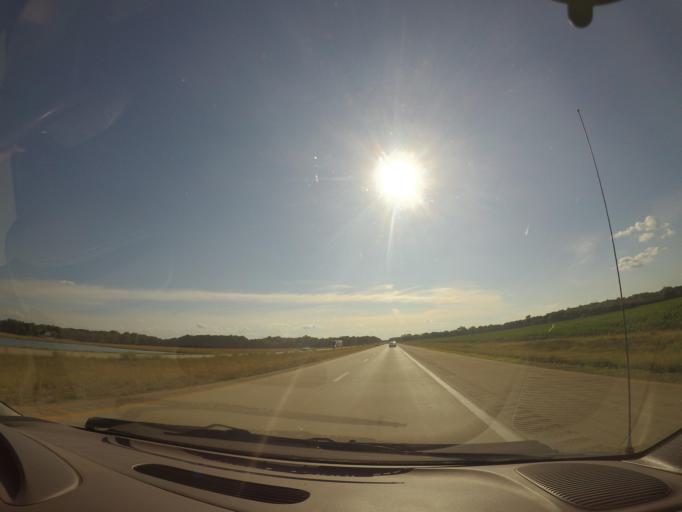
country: US
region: Ohio
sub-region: Henry County
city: Liberty Center
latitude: 41.4333
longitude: -83.9438
